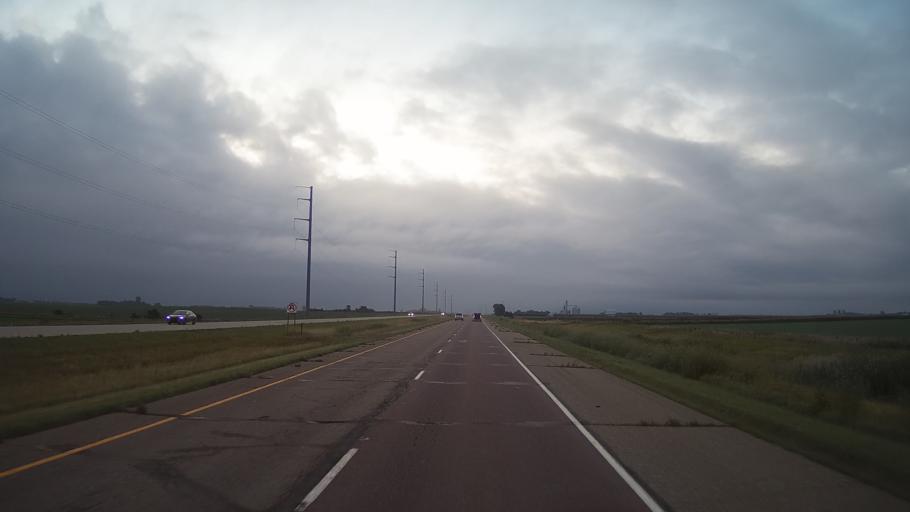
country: US
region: Iowa
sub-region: Dickinson County
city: Lake Park
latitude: 43.6374
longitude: -95.3583
